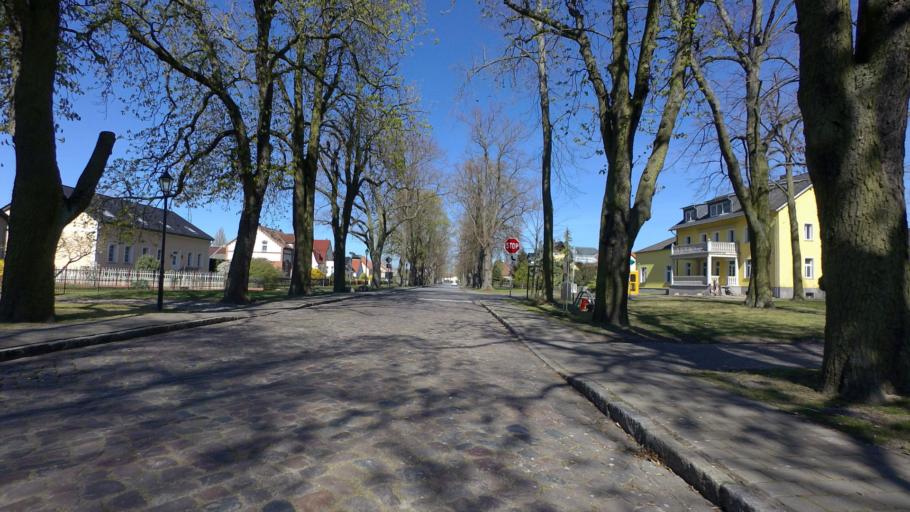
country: DE
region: Brandenburg
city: Rangsdorf
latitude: 52.3238
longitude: 13.4643
